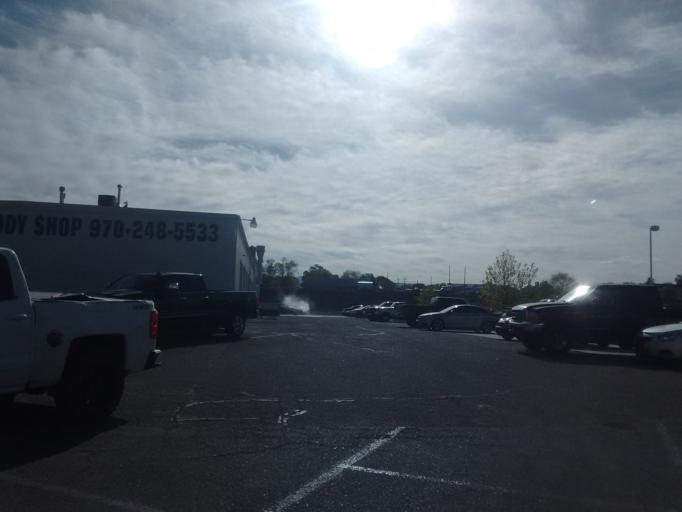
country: US
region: Colorado
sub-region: Mesa County
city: Grand Junction
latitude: 39.0756
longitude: -108.5743
